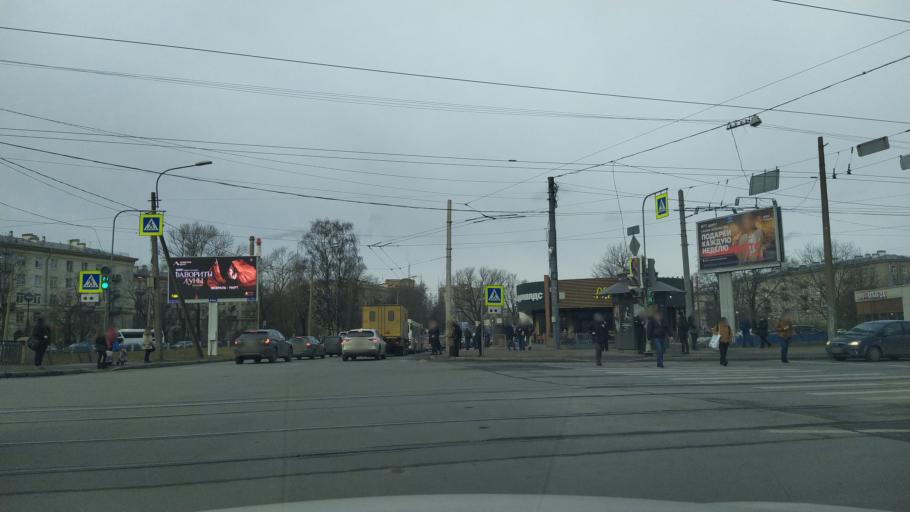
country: RU
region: Leningrad
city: Chernaya Rechka
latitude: 59.9864
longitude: 30.3031
